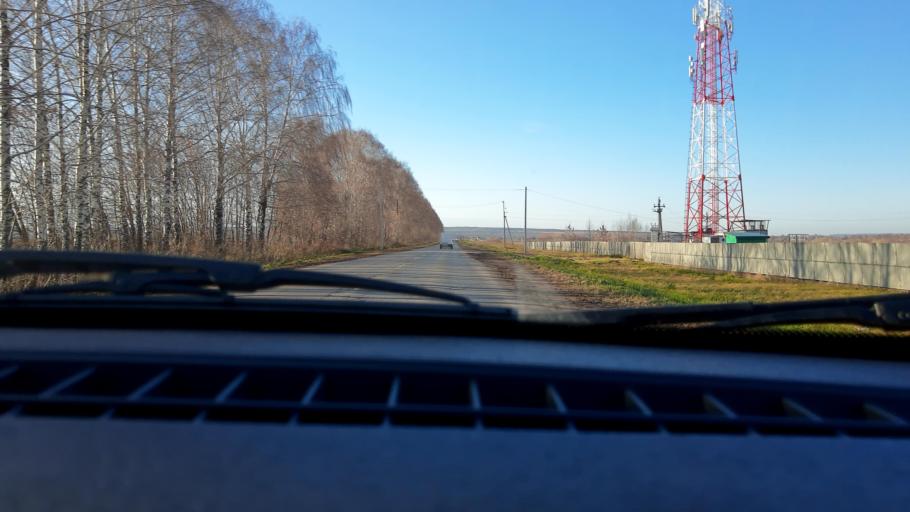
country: RU
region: Bashkortostan
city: Ufa
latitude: 54.8253
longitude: 55.9818
